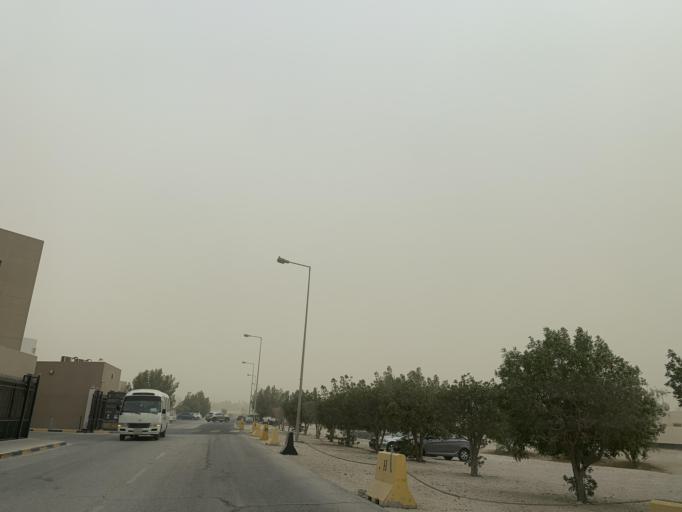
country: BH
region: Central Governorate
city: Madinat Hamad
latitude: 26.1351
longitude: 50.5215
